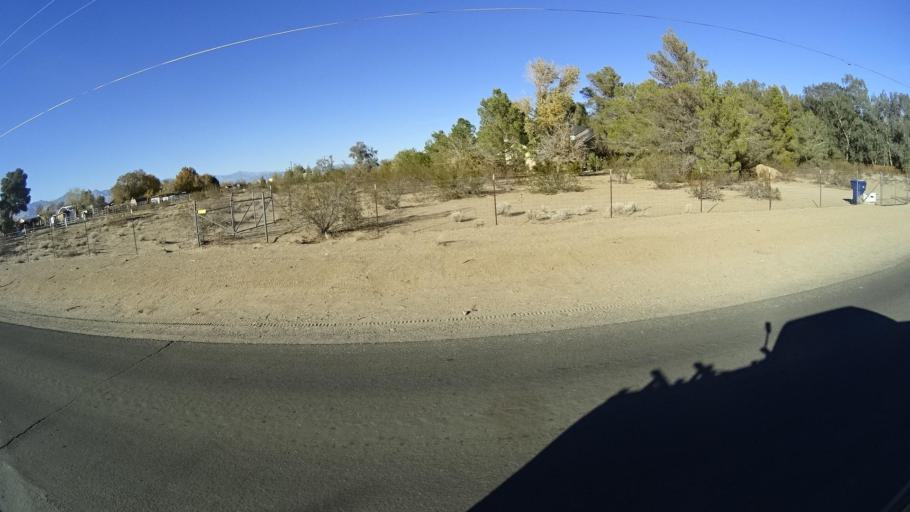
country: US
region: California
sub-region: Kern County
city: Ridgecrest
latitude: 35.6370
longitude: -117.7095
